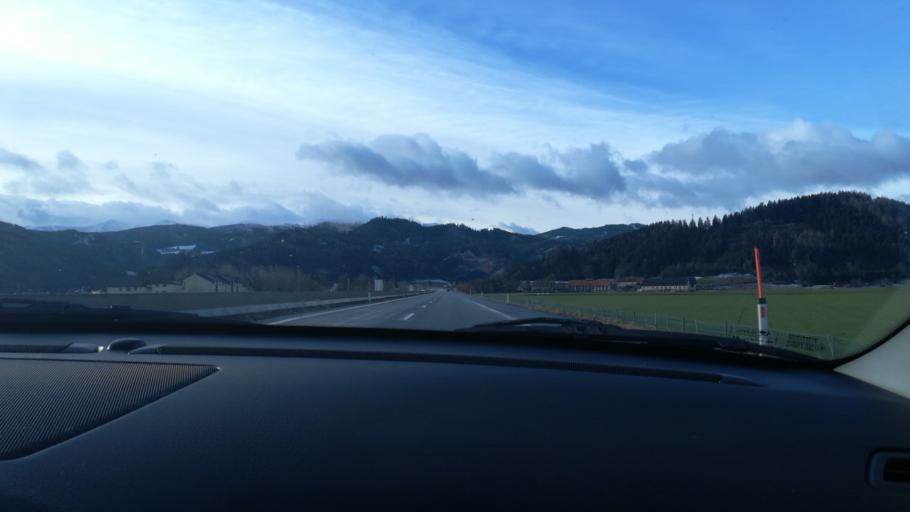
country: AT
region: Styria
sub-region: Politischer Bezirk Murtal
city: Judenburg
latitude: 47.1809
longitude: 14.6667
